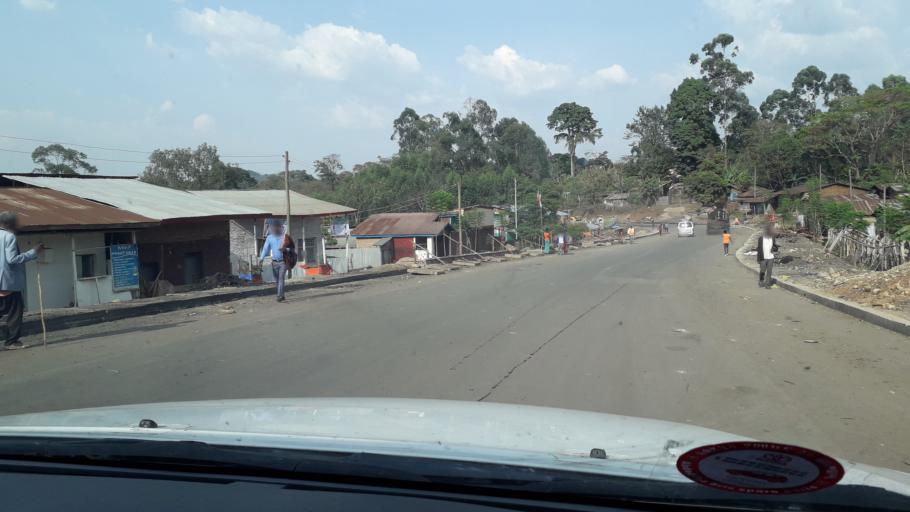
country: ET
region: Southern Nations, Nationalities, and People's Region
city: Mizan Teferi
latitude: 6.9339
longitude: 35.4982
